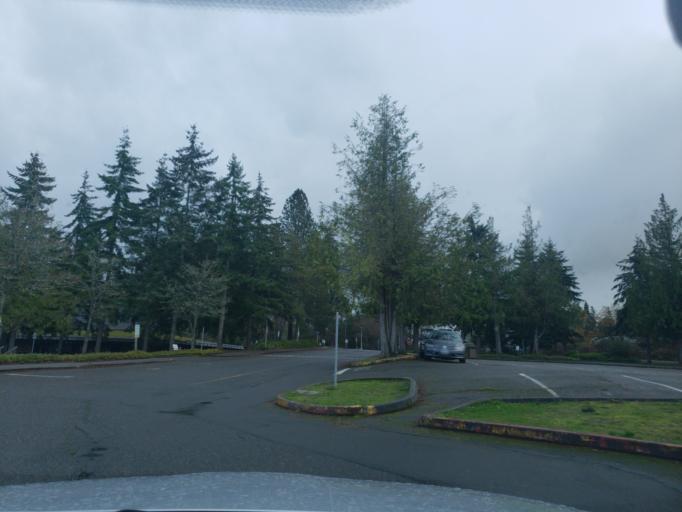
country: US
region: Washington
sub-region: King County
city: Shoreline
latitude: 47.7475
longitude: -122.3606
